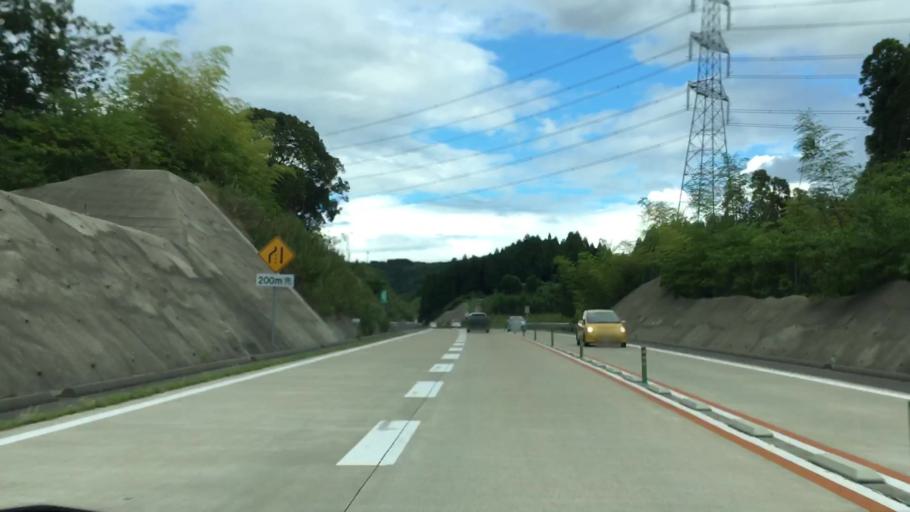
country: JP
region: Saga Prefecture
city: Imaricho-ko
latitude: 33.3555
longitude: 129.9268
